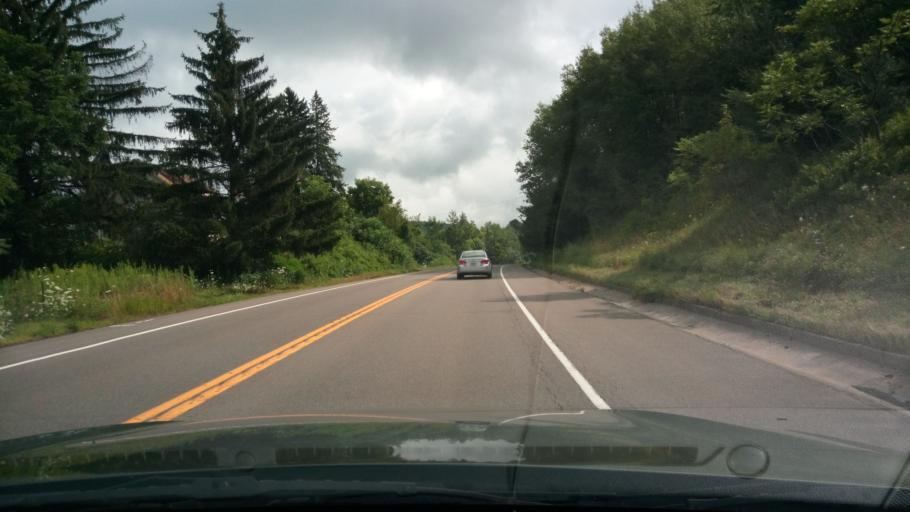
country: US
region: New York
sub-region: Tompkins County
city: Northwest Ithaca
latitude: 42.3484
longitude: -76.6169
